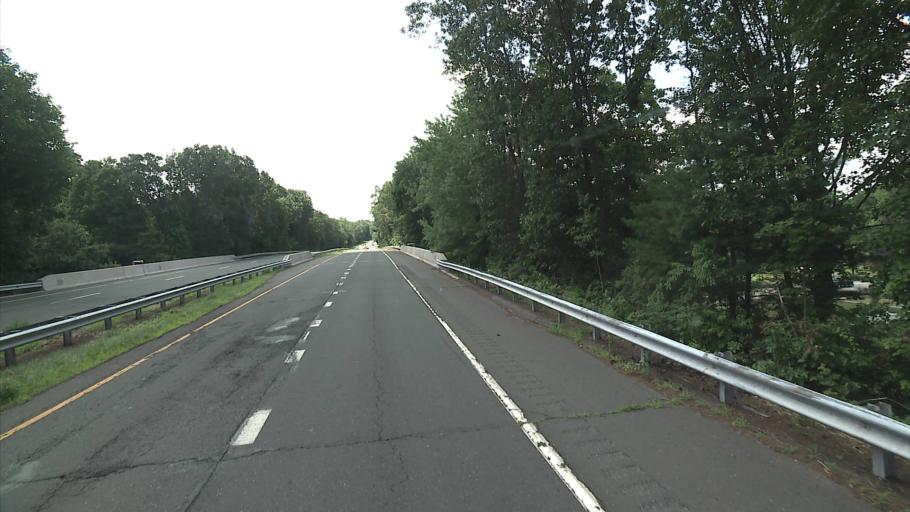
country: US
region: Connecticut
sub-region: Hartford County
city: Glastonbury Center
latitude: 41.7020
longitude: -72.6009
